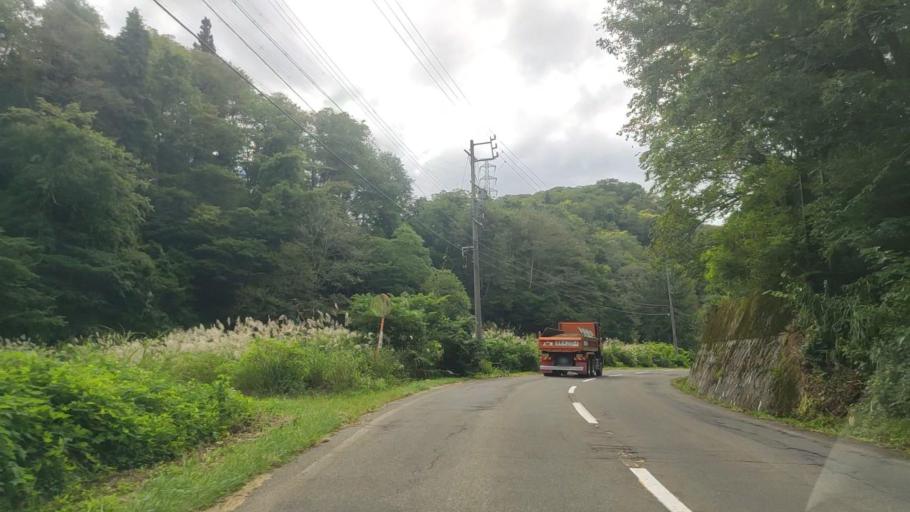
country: JP
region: Nagano
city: Iiyama
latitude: 36.8875
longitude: 138.3232
